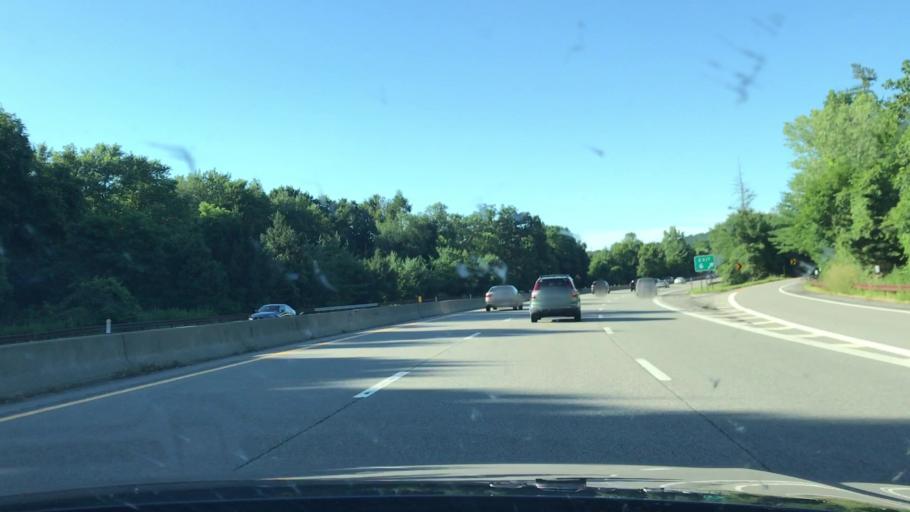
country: US
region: New York
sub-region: Westchester County
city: Briarcliff Manor
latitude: 41.1403
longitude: -73.8170
